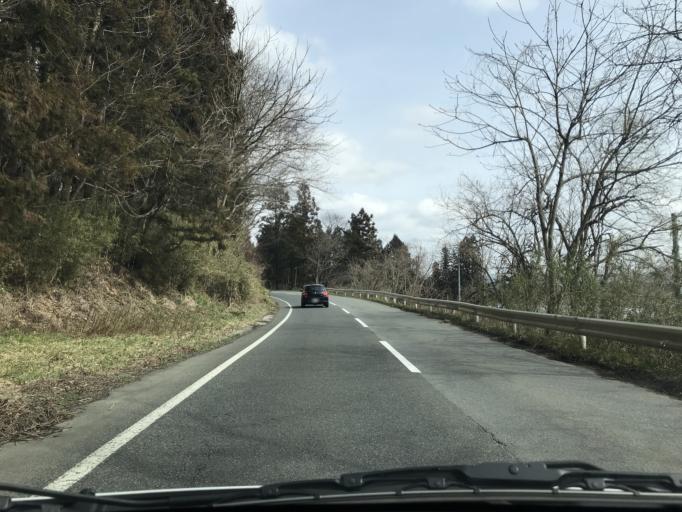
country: JP
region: Iwate
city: Mizusawa
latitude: 39.2127
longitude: 141.2098
